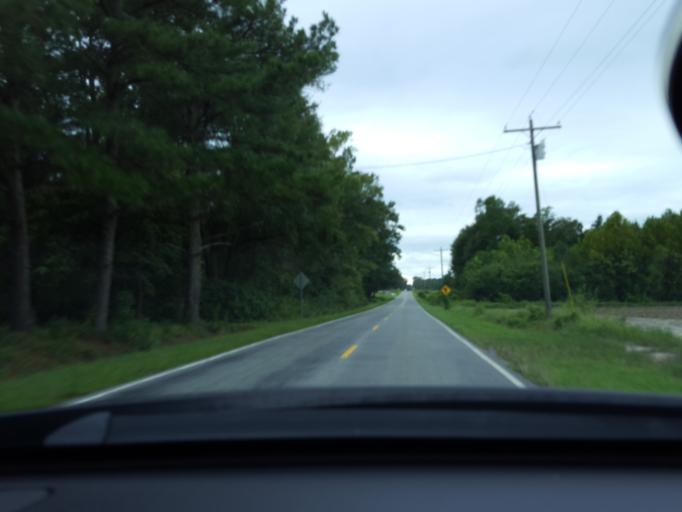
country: US
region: North Carolina
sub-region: Sampson County
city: Clinton
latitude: 34.7777
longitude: -78.3380
